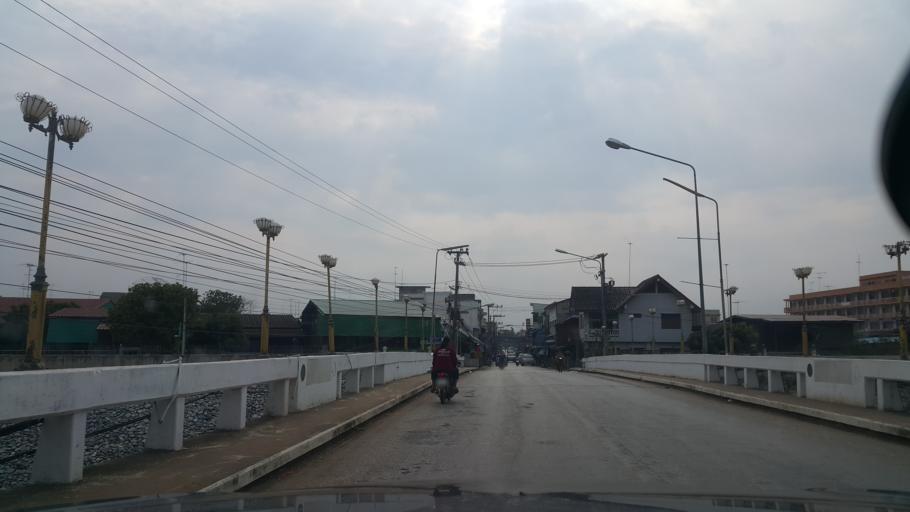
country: TH
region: Sukhothai
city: Si Samrong
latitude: 17.1690
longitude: 99.8609
